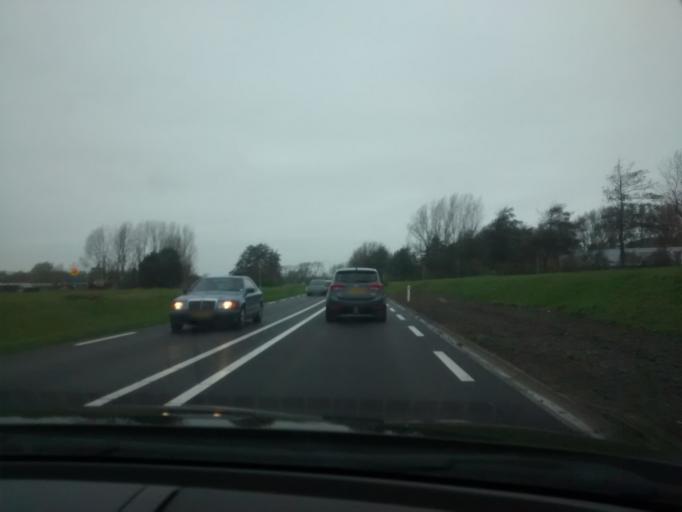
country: NL
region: South Holland
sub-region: Gemeente Katwijk
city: Katwijk aan den Rijn
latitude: 52.1826
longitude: 4.4231
